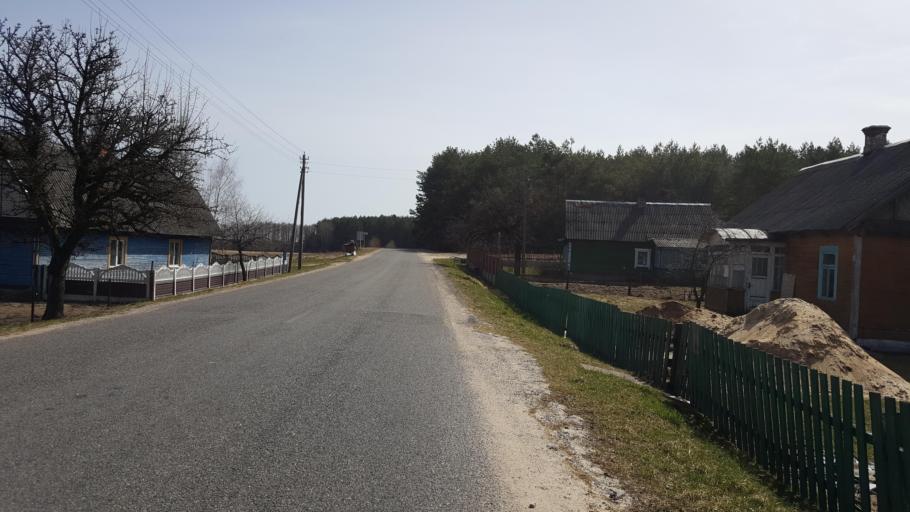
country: BY
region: Brest
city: Kamyanyuki
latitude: 52.5186
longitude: 23.8506
